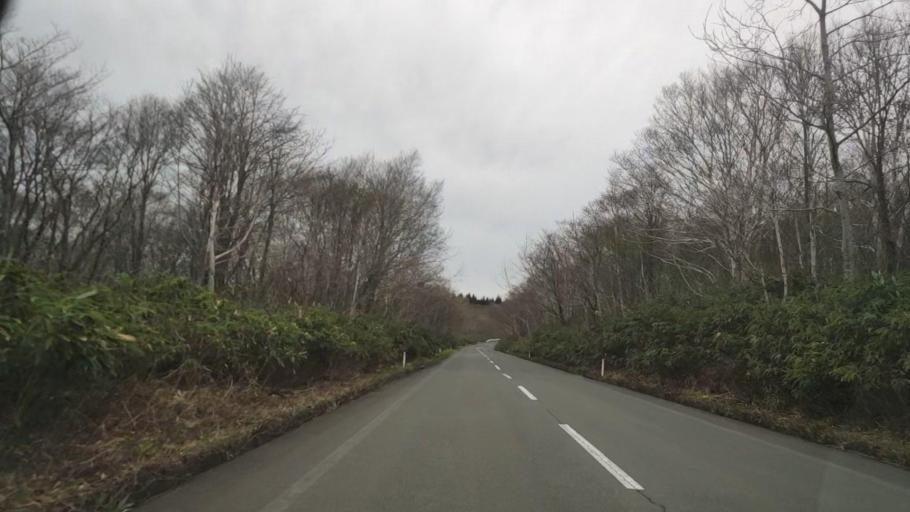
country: JP
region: Akita
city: Hanawa
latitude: 40.4076
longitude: 140.8517
